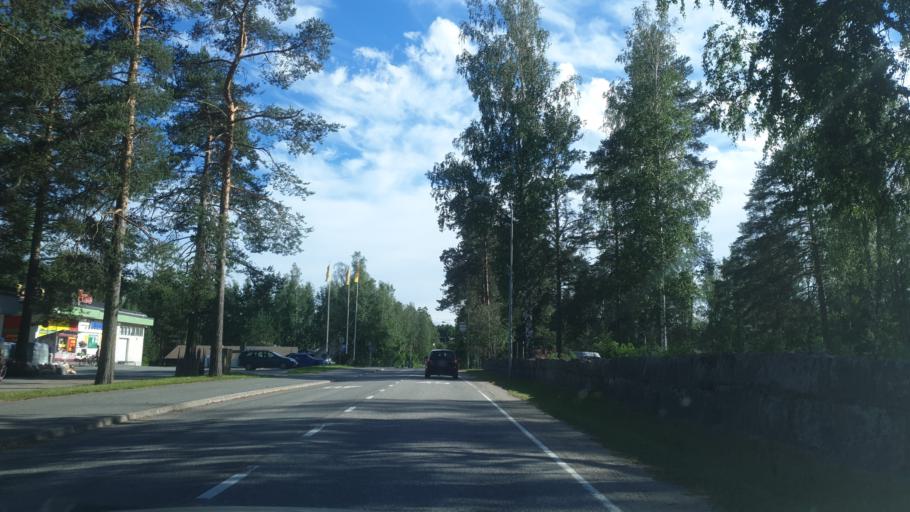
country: FI
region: Southern Savonia
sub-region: Mikkeli
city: Pertunmaa
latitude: 61.5066
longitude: 26.4818
